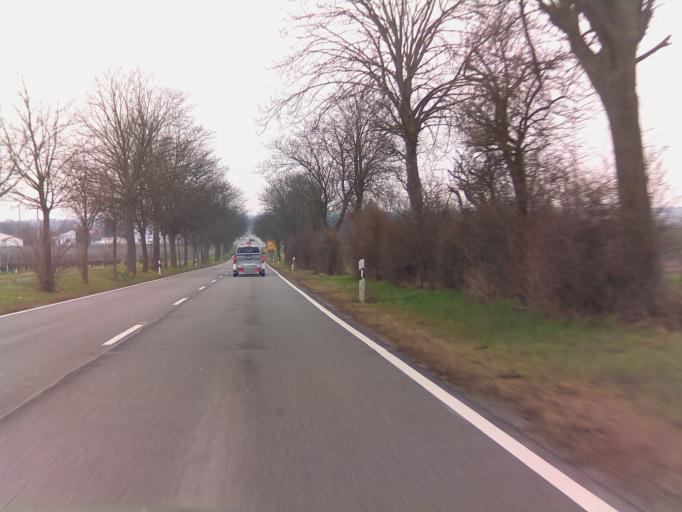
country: DE
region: Rheinland-Pfalz
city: Schornsheim
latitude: 49.8424
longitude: 8.1832
